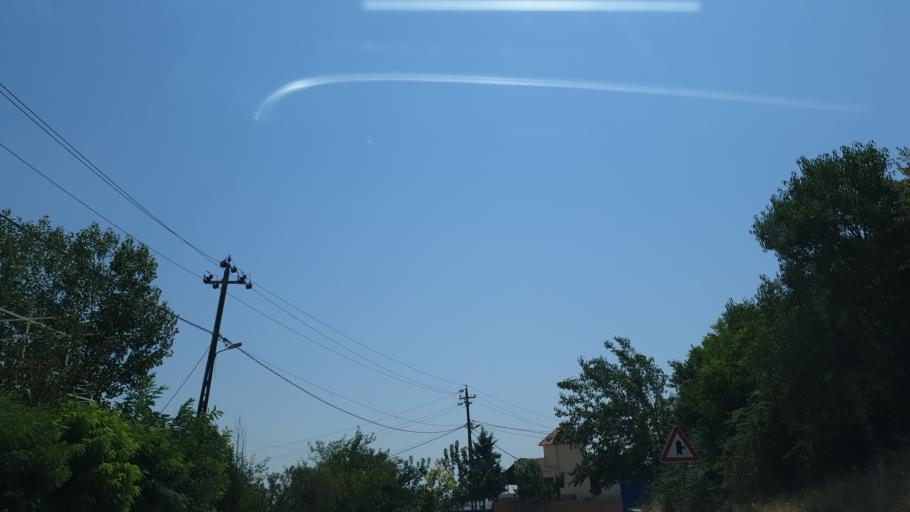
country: IQ
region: Arbil
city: Nahiyat Hiran
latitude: 36.2829
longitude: 44.4918
